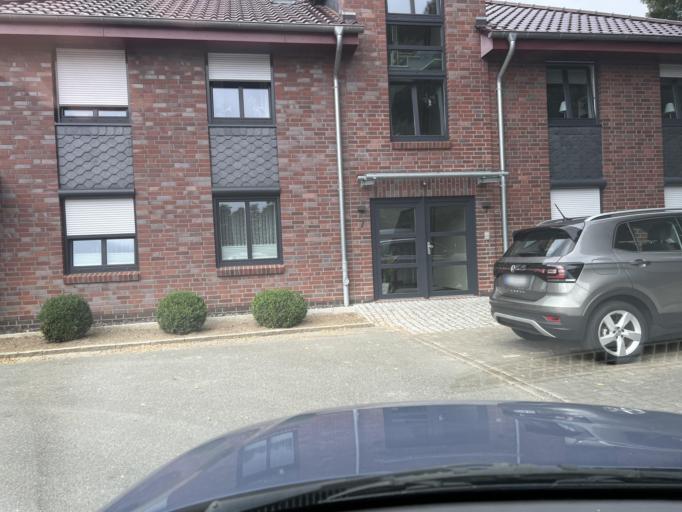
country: DE
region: Schleswig-Holstein
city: Heide
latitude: 54.1915
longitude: 9.0994
